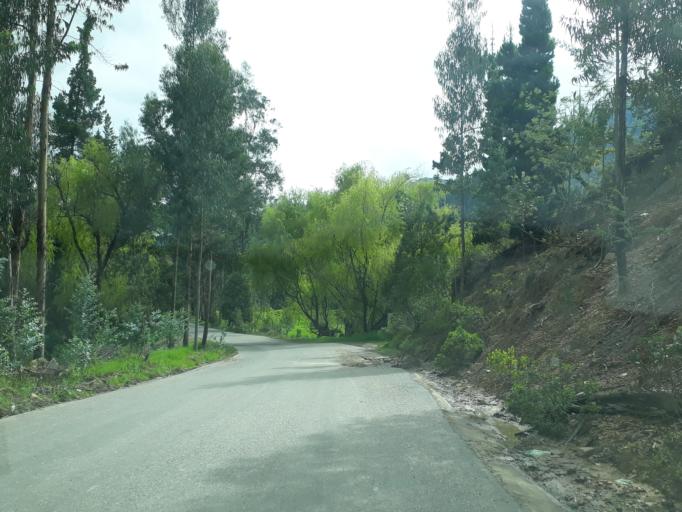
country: CO
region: Cundinamarca
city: Cucunuba
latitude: 5.2418
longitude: -73.7705
